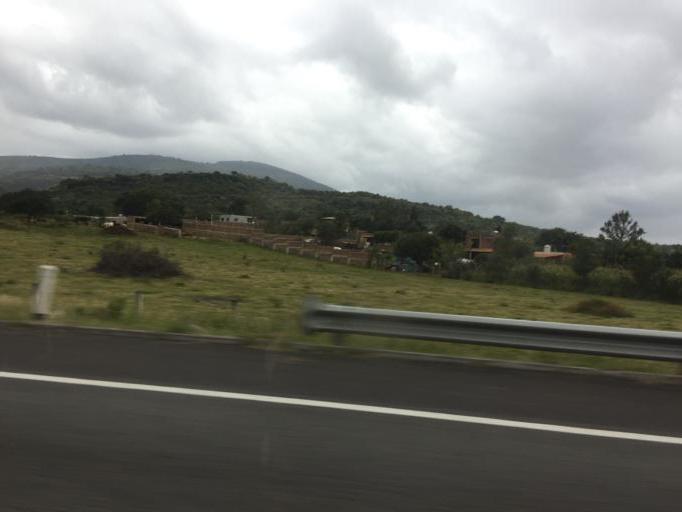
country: MX
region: Jalisco
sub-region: Zapotlanejo
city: La Mezquitera
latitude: 20.5413
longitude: -103.0245
